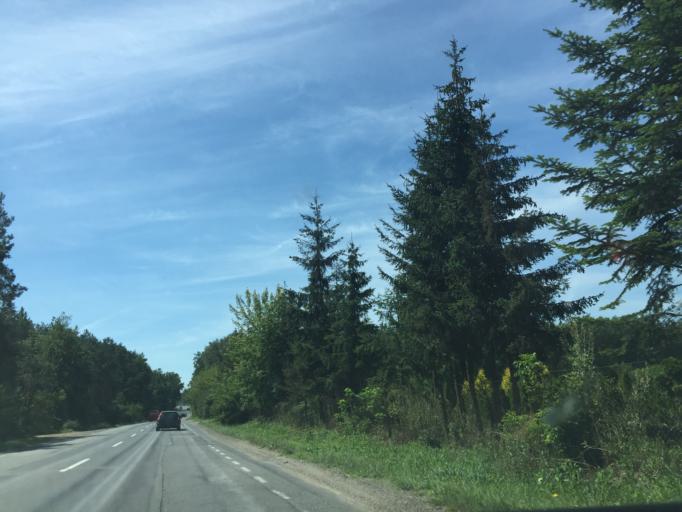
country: PL
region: Lodz Voivodeship
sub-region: Piotrkow Trybunalski
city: Piotrkow Trybunalski
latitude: 51.4355
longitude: 19.7193
